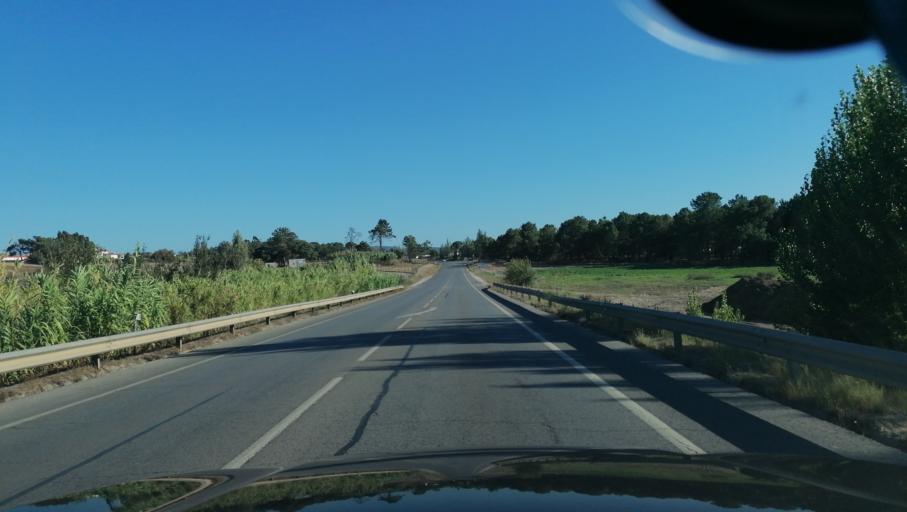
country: PT
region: Setubal
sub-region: Moita
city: Moita
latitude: 38.6386
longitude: -8.9714
